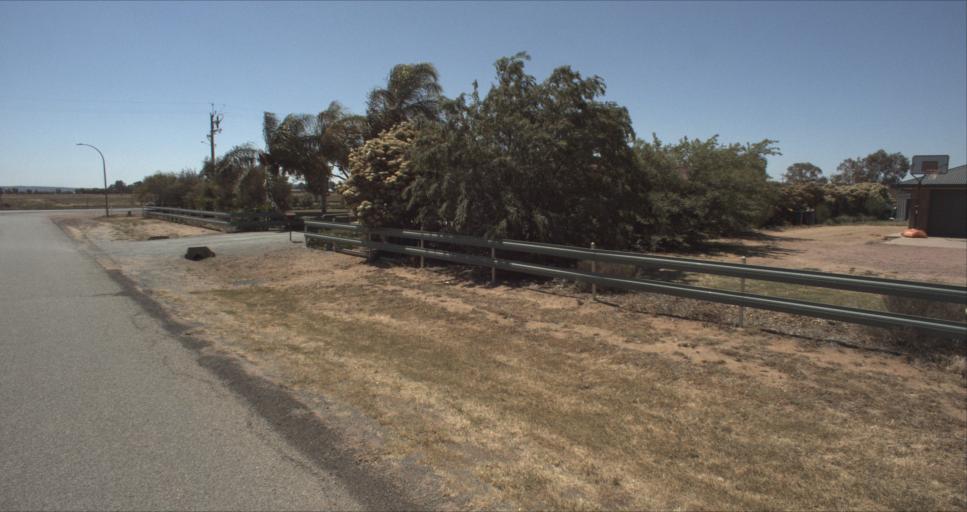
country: AU
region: New South Wales
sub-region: Leeton
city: Leeton
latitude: -34.5286
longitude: 146.3987
